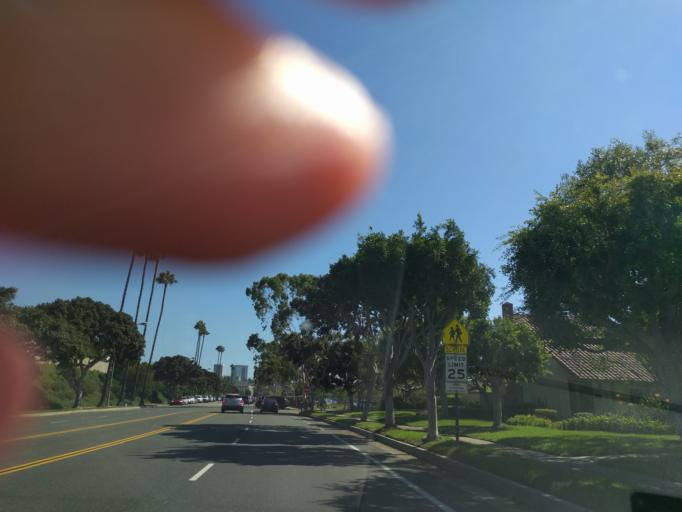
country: US
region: California
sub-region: Orange County
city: Costa Mesa
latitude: 33.6369
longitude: -117.8765
